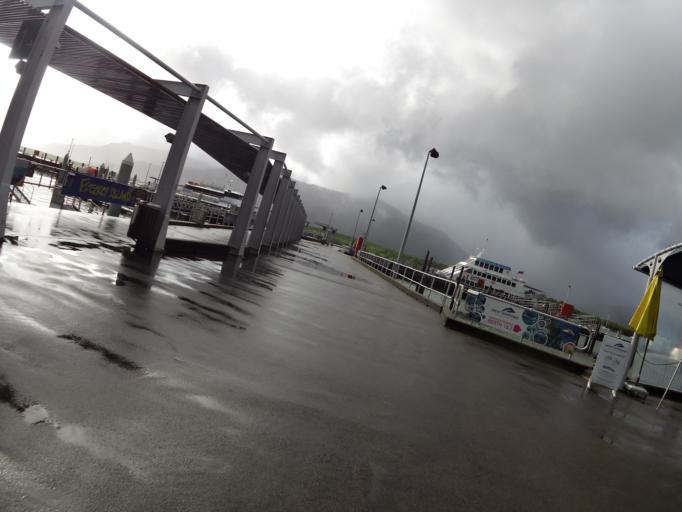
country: AU
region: Queensland
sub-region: Cairns
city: Cairns
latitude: -16.9214
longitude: 145.7813
